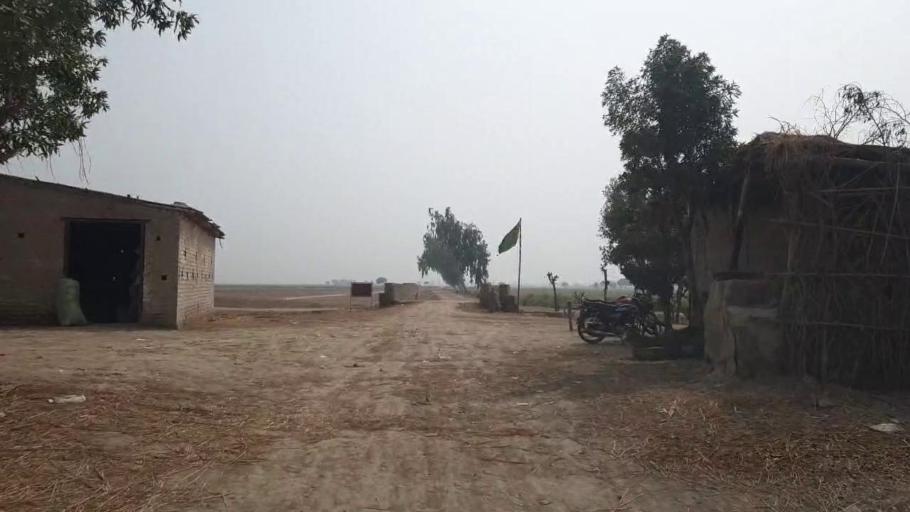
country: PK
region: Sindh
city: Kario
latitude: 24.6320
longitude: 68.5958
